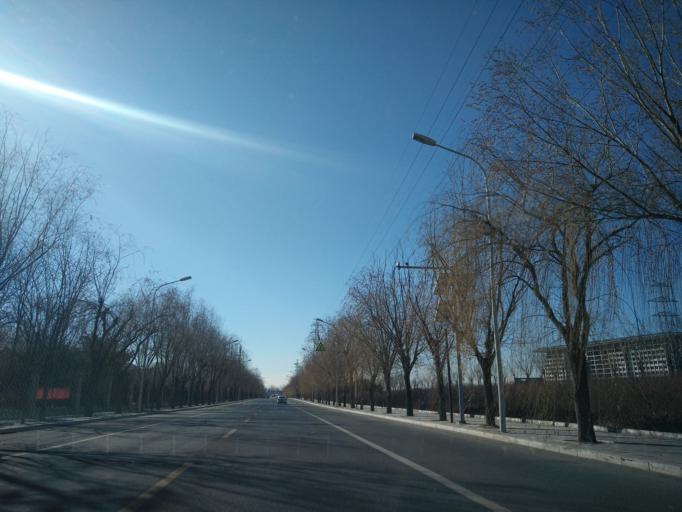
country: CN
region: Beijing
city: Qingyundian
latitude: 39.7481
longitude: 116.5279
